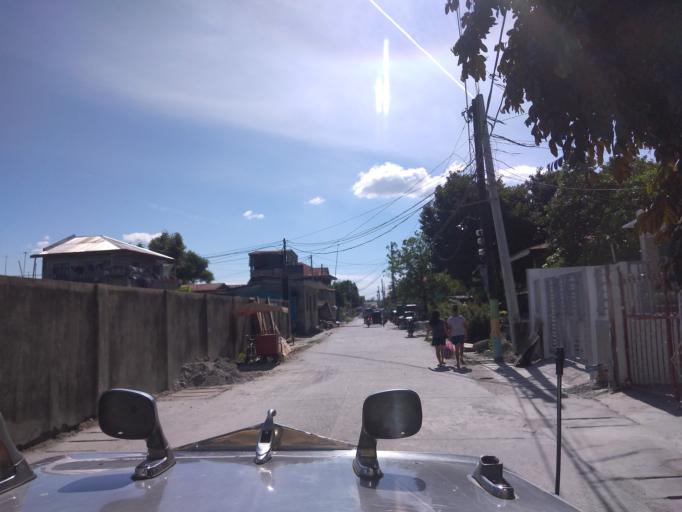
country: PH
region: Central Luzon
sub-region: Province of Pampanga
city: San Agustin
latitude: 14.9914
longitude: 120.6016
